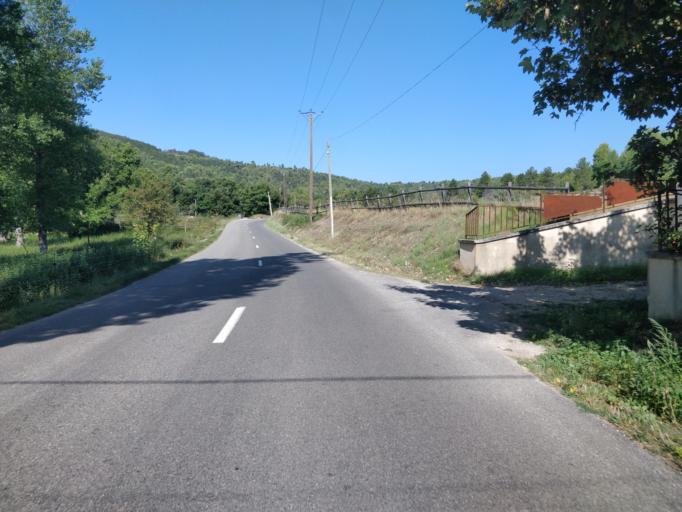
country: FR
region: Provence-Alpes-Cote d'Azur
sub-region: Departement des Alpes-de-Haute-Provence
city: Riez
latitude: 43.8440
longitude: 6.2071
